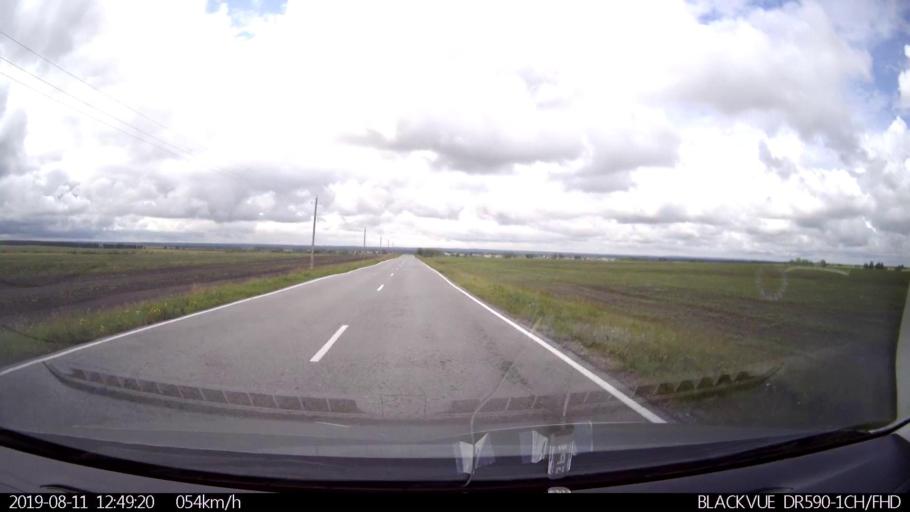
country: RU
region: Ulyanovsk
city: Ignatovka
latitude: 53.8746
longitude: 47.6882
